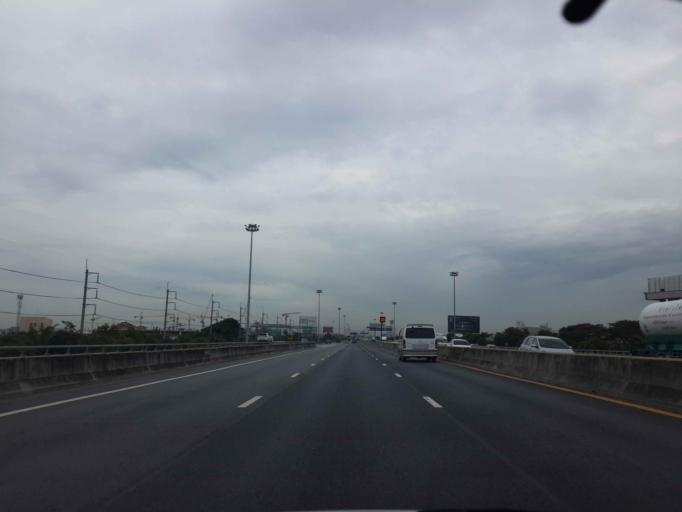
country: TH
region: Bangkok
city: Wang Thonglang
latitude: 13.7950
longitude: 100.6124
